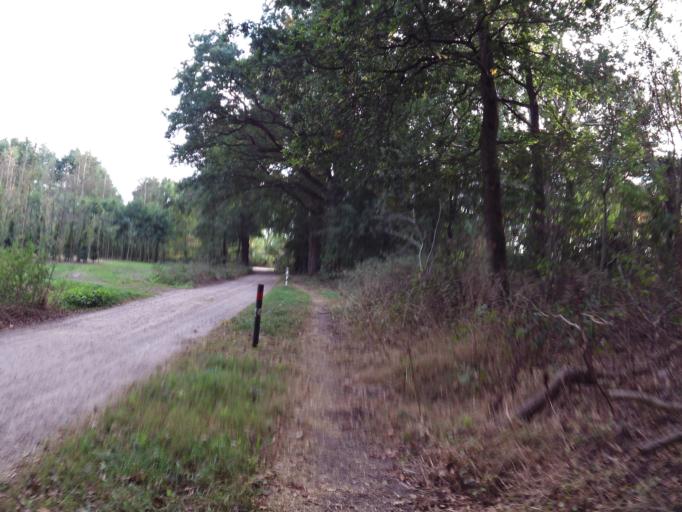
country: NL
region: North Brabant
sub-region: Gemeente Vught
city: Vught
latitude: 51.6601
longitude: 5.2446
